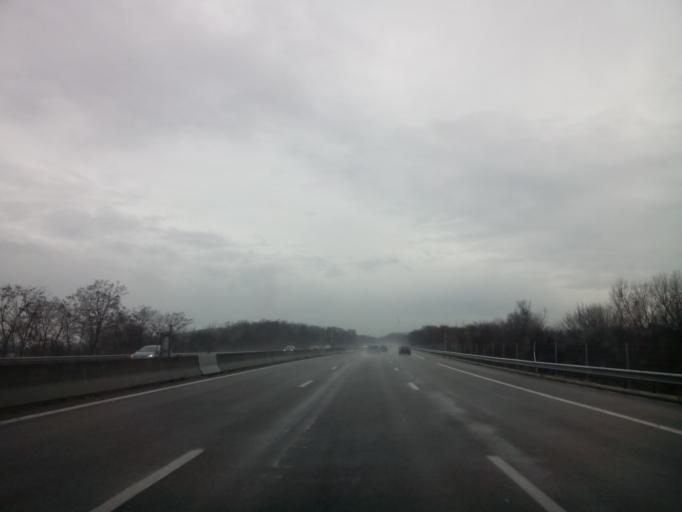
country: FR
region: Rhone-Alpes
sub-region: Departement de la Drome
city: Beausemblant
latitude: 45.2384
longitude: 4.8456
